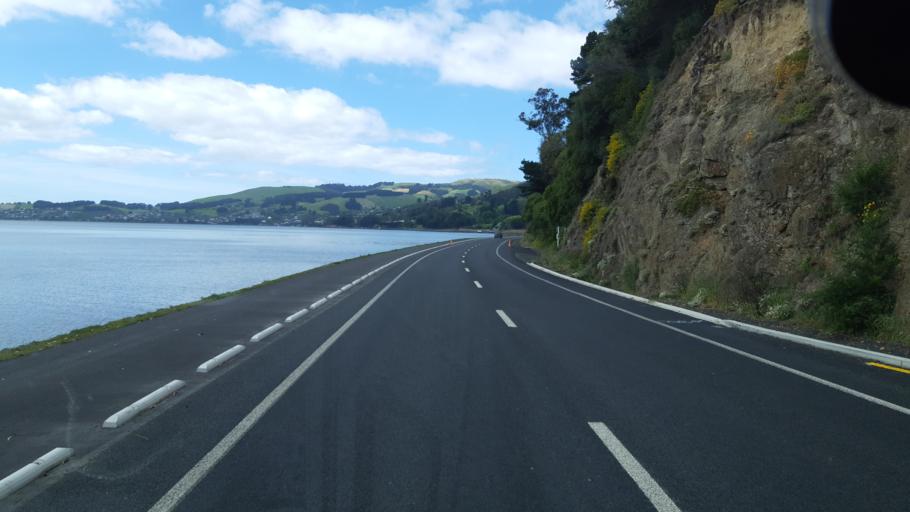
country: NZ
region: Otago
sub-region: Dunedin City
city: Dunedin
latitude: -45.8796
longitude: 170.5613
